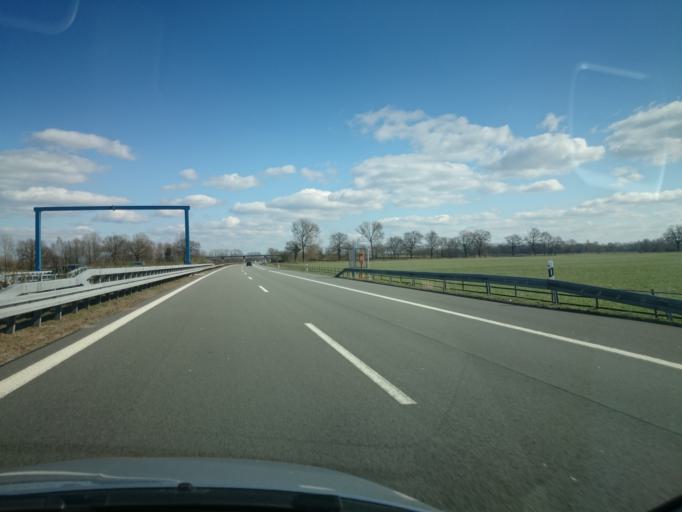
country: DE
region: Mecklenburg-Vorpommern
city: Neustadt-Glewe
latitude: 53.4169
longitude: 11.5446
